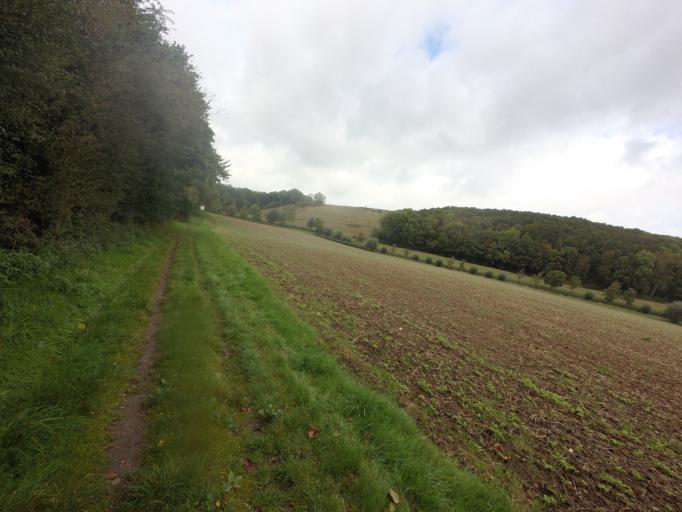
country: NL
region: Limburg
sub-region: Eijsden-Margraten
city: Margraten
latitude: 50.8061
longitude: 5.8626
